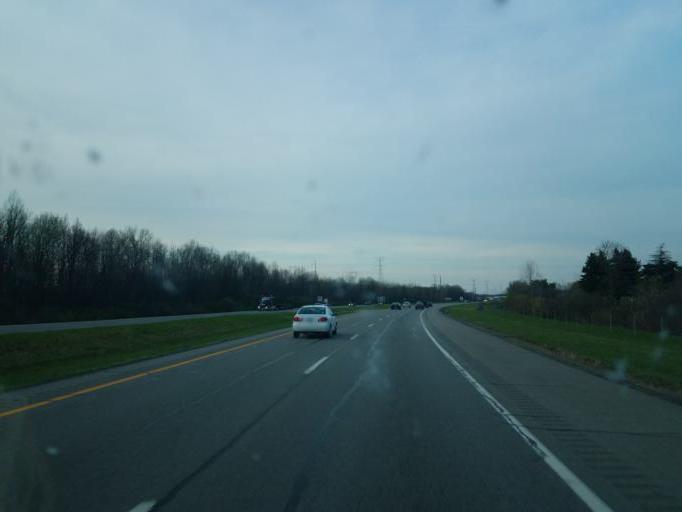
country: US
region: Ohio
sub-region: Lorain County
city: Sheffield
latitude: 41.4328
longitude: -82.0824
